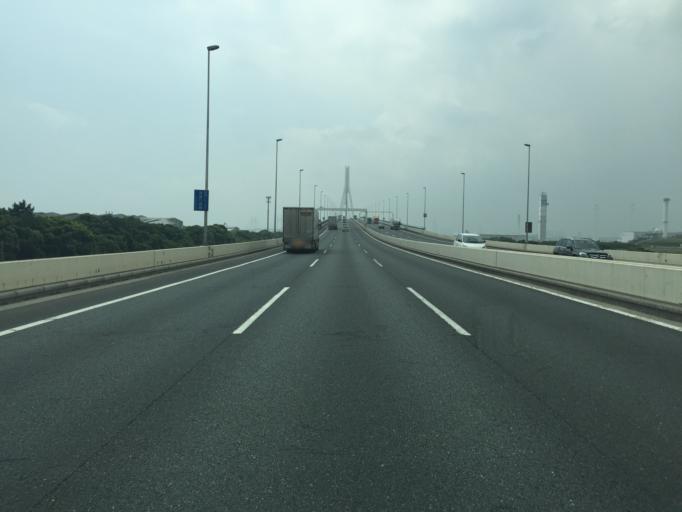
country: JP
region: Kanagawa
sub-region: Kawasaki-shi
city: Kawasaki
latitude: 35.4790
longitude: 139.7151
